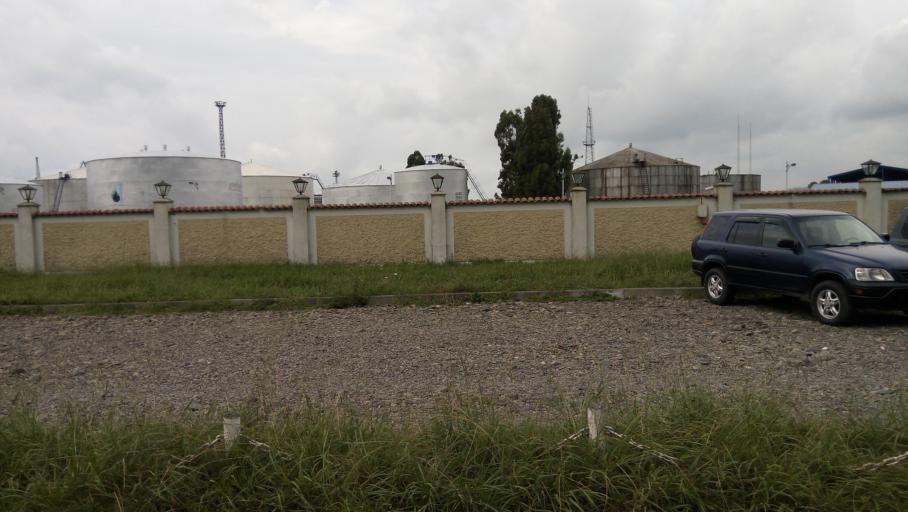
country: GE
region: Ajaria
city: Batumi
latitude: 41.6426
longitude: 41.6585
